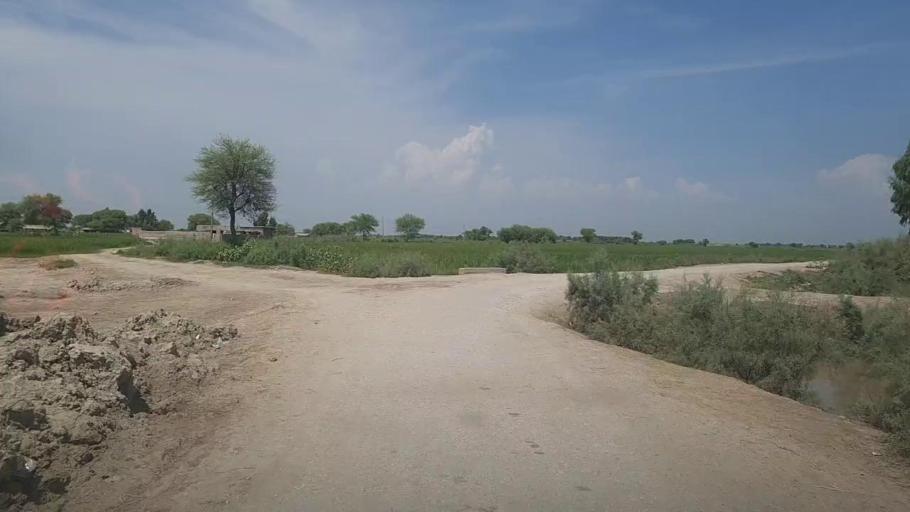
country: PK
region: Sindh
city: Kandhkot
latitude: 28.2797
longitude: 69.2347
